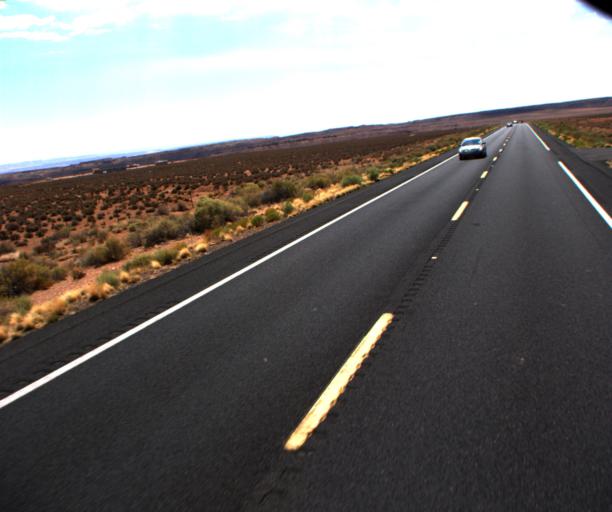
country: US
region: Arizona
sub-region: Coconino County
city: Tuba City
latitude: 35.8929
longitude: -111.5355
